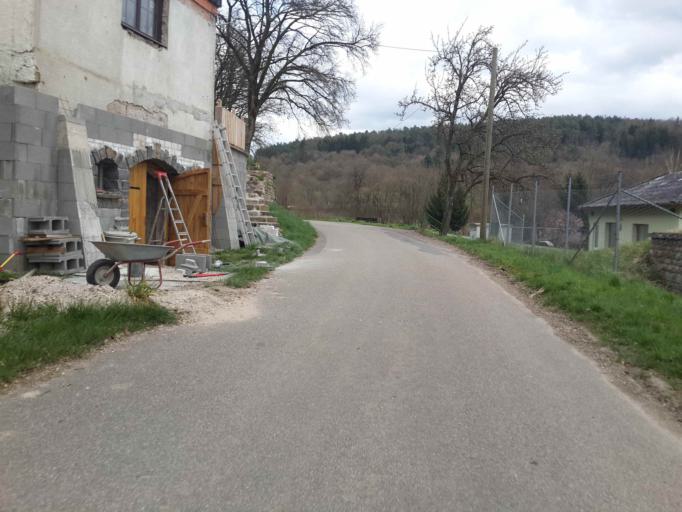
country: DE
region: Baden-Wuerttemberg
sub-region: Regierungsbezirk Stuttgart
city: Roigheim
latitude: 49.3780
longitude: 9.3687
